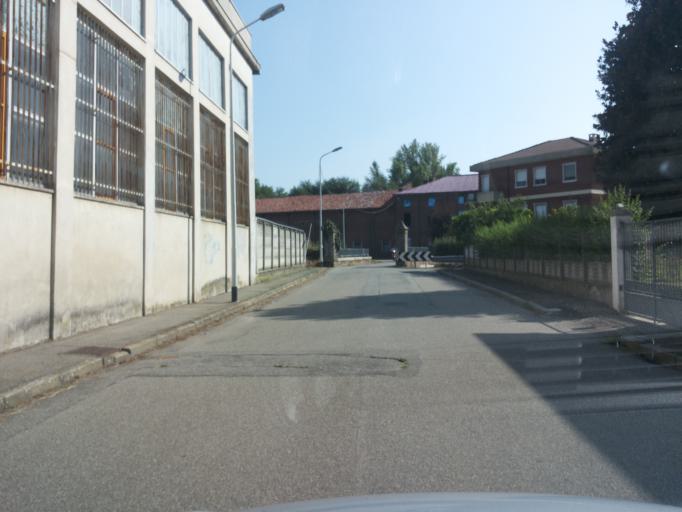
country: IT
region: Piedmont
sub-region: Provincia di Vercelli
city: Vercelli
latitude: 45.3225
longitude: 8.4011
